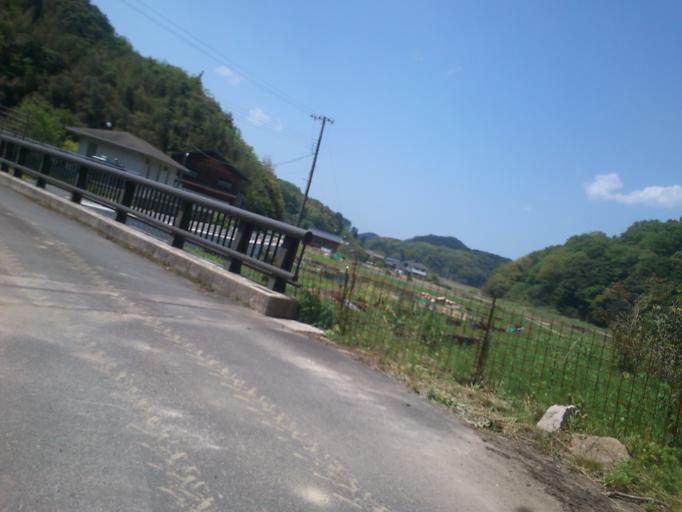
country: JP
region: Kyoto
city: Miyazu
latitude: 35.7066
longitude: 135.1178
